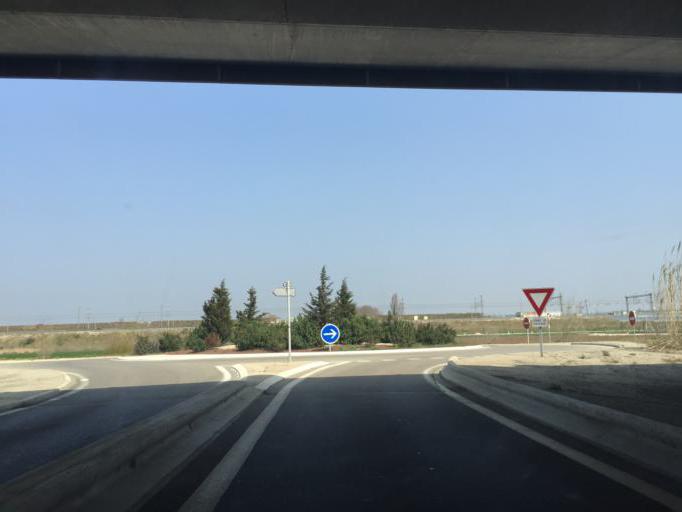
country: FR
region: Provence-Alpes-Cote d'Azur
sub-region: Departement des Bouches-du-Rhone
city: Barbentane
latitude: 43.9227
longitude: 4.7763
